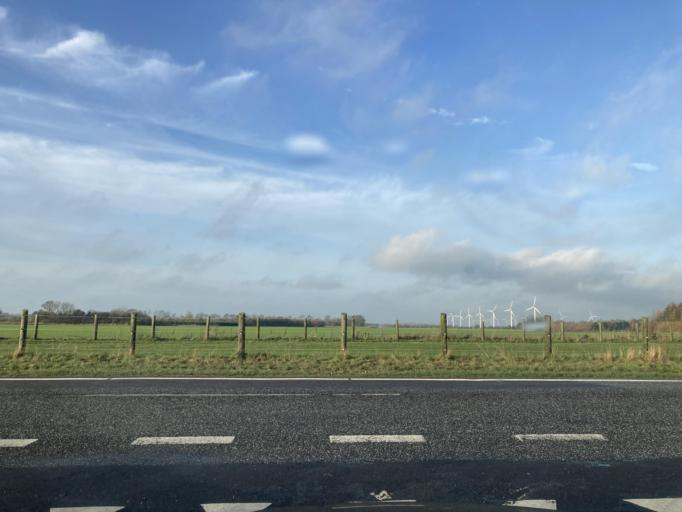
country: DK
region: Zealand
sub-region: Lolland Kommune
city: Rodby
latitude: 54.6903
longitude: 11.3702
